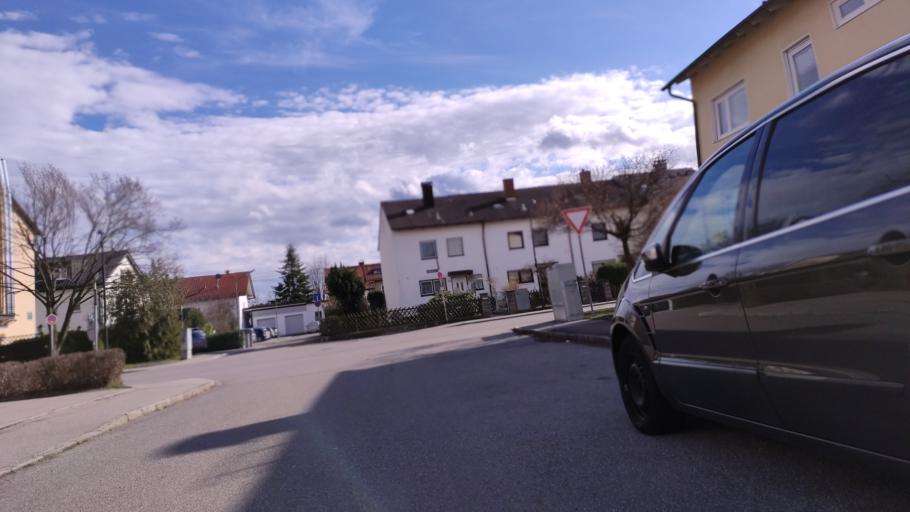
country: DE
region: Bavaria
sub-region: Upper Bavaria
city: Emmering
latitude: 48.1885
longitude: 11.2796
